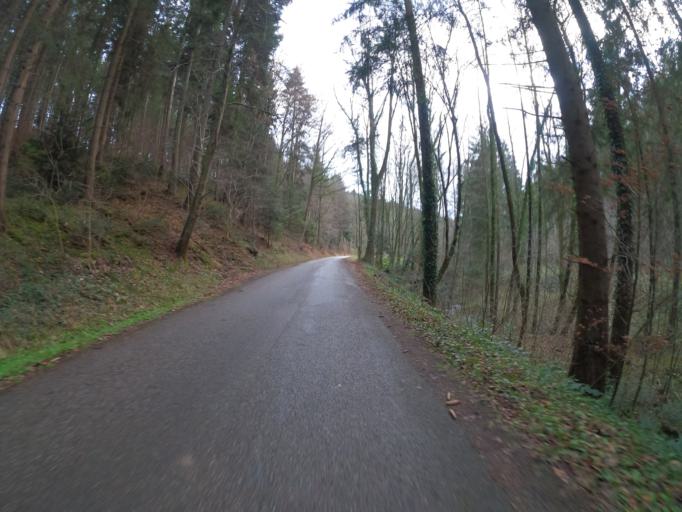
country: DE
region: Baden-Wuerttemberg
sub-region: Regierungsbezirk Stuttgart
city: Lorch
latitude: 48.7823
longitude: 9.7223
